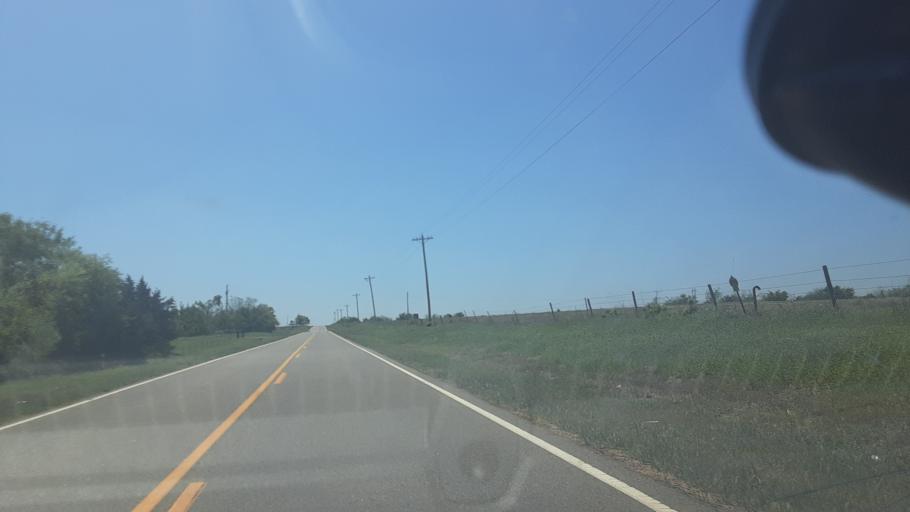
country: US
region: Oklahoma
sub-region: Logan County
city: Guthrie
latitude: 36.0251
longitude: -97.4076
